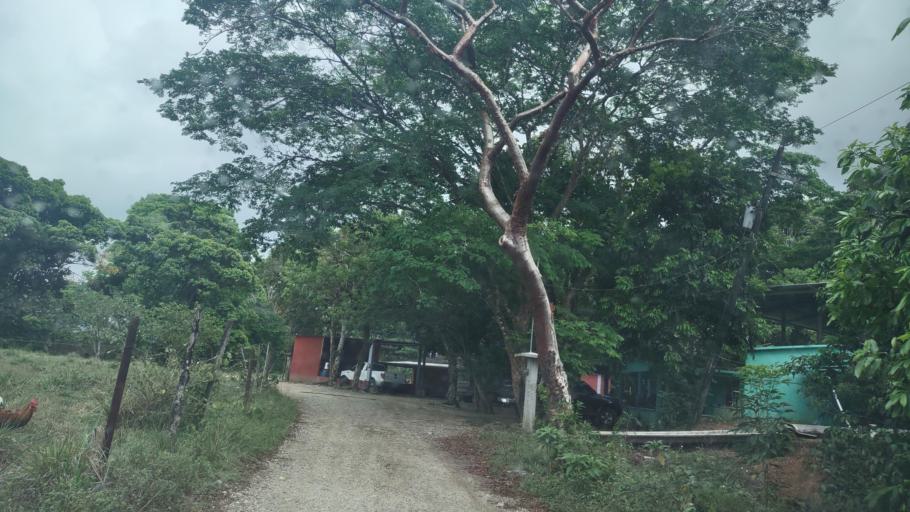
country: MX
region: Veracruz
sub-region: Uxpanapa
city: Poblado 10
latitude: 17.4981
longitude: -94.1598
